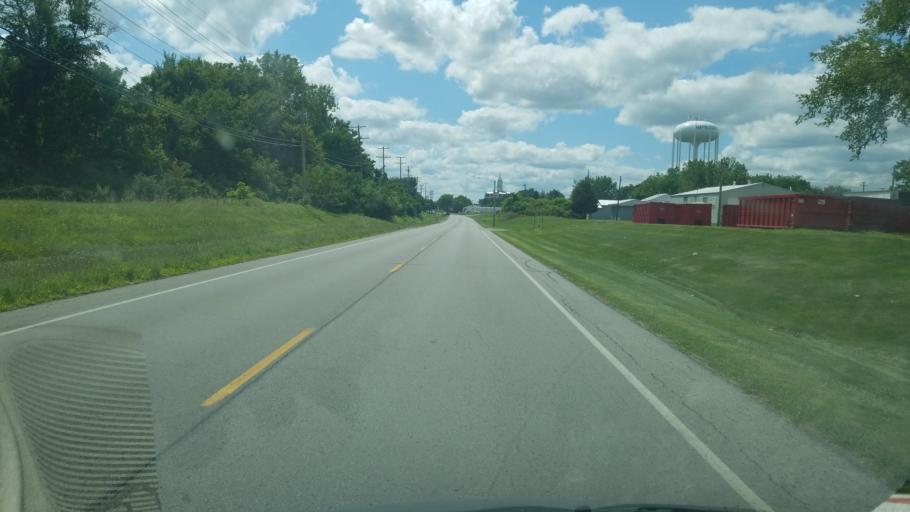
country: US
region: Ohio
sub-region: Henry County
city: Napoleon
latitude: 41.3974
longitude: -84.1161
